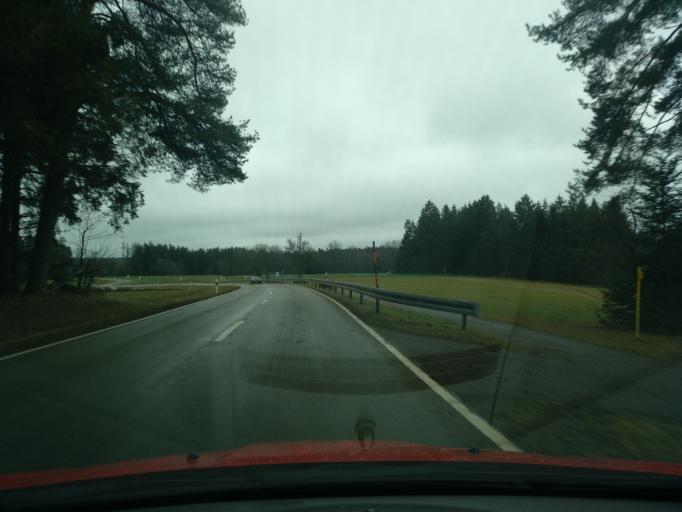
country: DE
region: Baden-Wuerttemberg
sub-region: Freiburg Region
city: Sankt Georgen im Schwarzwald
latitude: 48.1417
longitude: 8.3264
